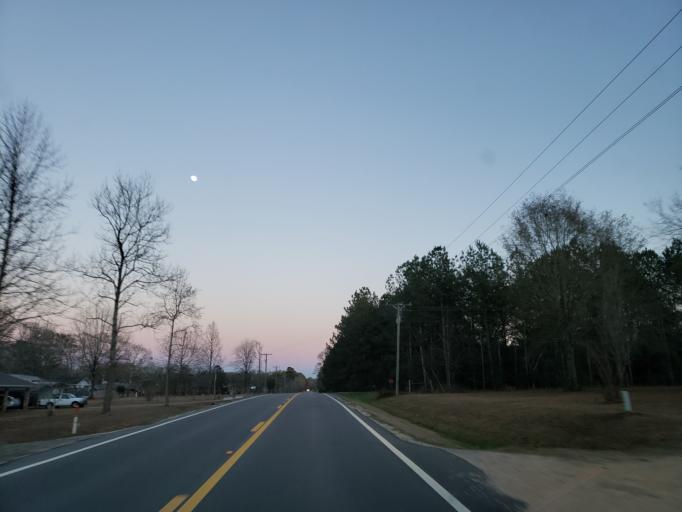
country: US
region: Mississippi
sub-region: Jones County
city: Ellisville
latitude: 31.5798
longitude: -89.2628
